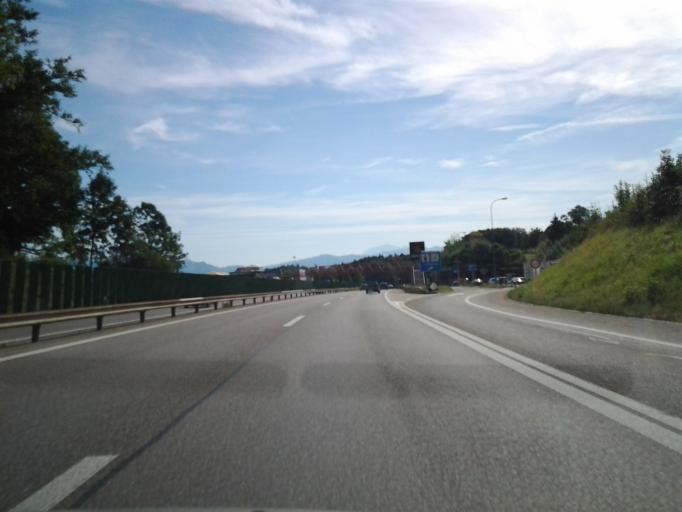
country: CH
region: Schwyz
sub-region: Bezirk Hoefe
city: Feusisberg
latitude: 47.1956
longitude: 8.7490
